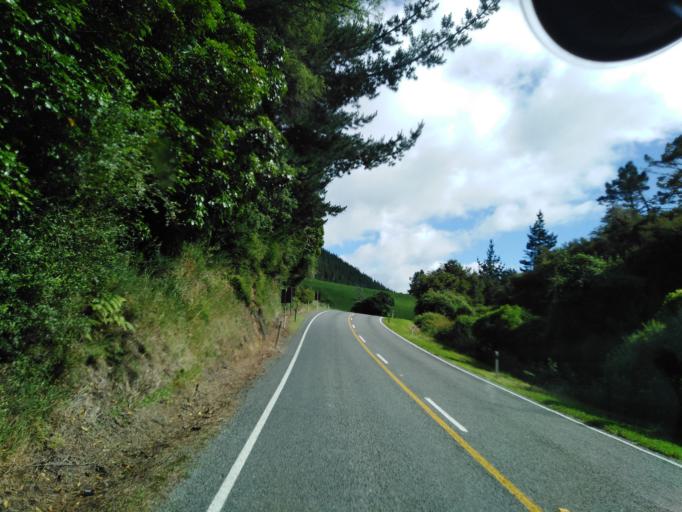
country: NZ
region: Nelson
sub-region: Nelson City
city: Nelson
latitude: -41.2894
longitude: 173.5716
